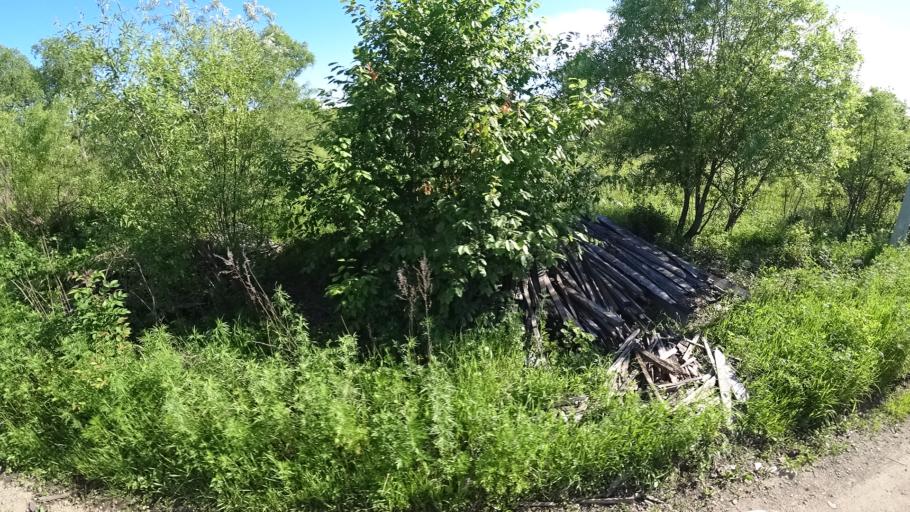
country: RU
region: Khabarovsk Krai
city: Khor
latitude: 47.8843
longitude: 135.0246
